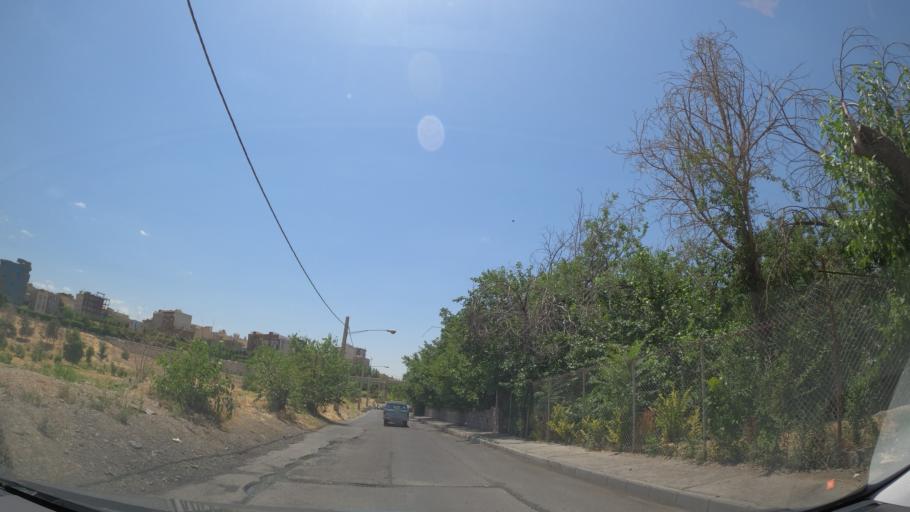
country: IR
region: Tehran
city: Tajrish
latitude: 35.7801
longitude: 51.3899
